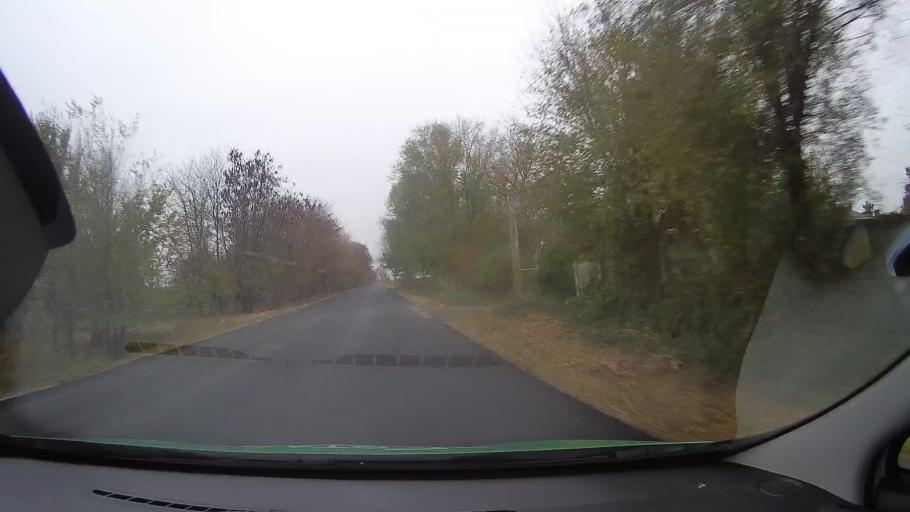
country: RO
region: Ialomita
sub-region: Comuna Valea Ciorii
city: Valea Ciorii
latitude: 44.7425
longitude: 27.5754
